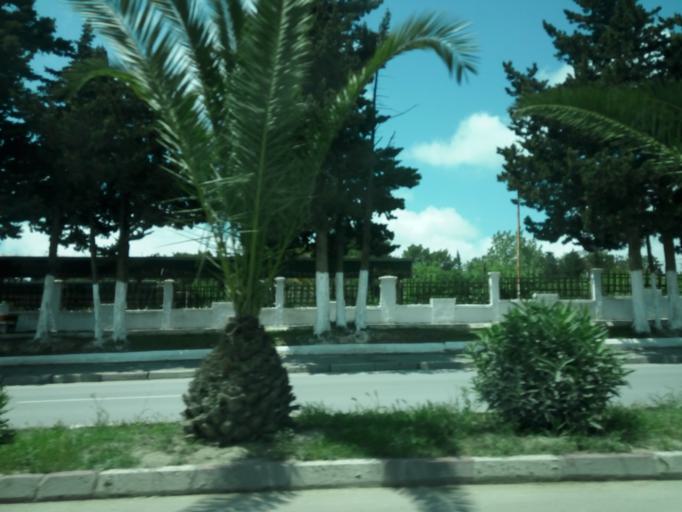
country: DZ
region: Tipaza
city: Saoula
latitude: 36.7279
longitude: 2.9912
